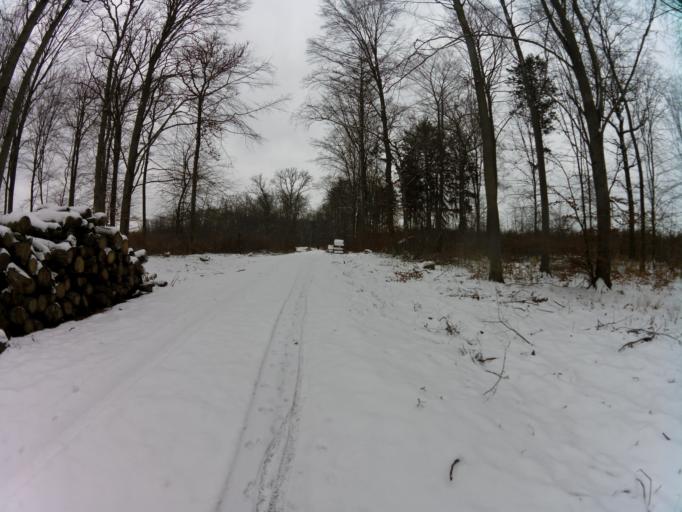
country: PL
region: West Pomeranian Voivodeship
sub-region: Powiat choszczenski
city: Recz
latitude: 53.3194
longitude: 15.5527
